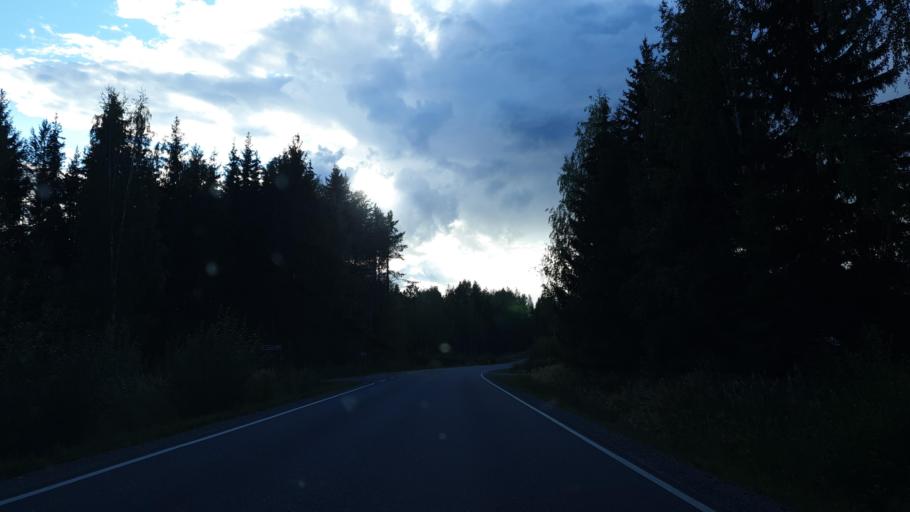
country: FI
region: Northern Savo
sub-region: Koillis-Savo
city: Juankoski
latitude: 63.2020
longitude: 28.2884
